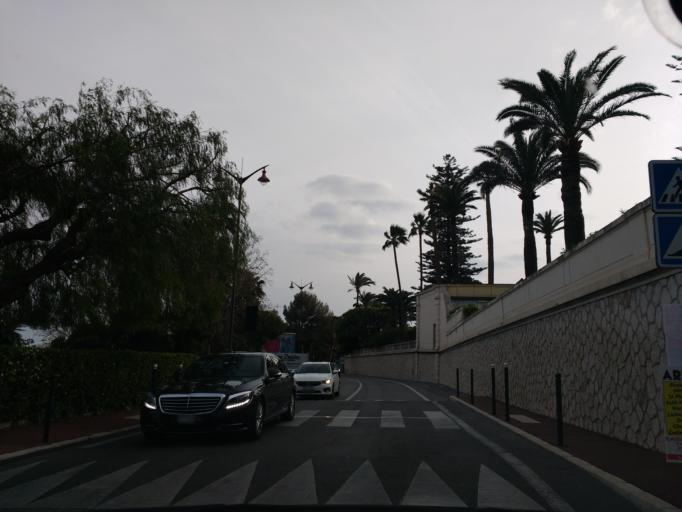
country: FR
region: Provence-Alpes-Cote d'Azur
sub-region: Departement des Alpes-Maritimes
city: Beaulieu-sur-Mer
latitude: 43.7114
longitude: 7.3358
